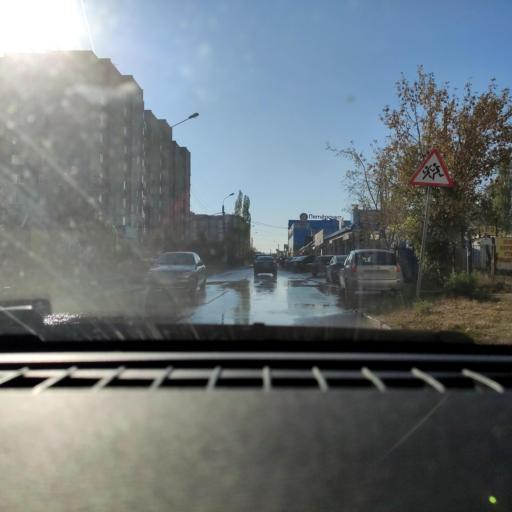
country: RU
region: Voronezj
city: Somovo
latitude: 51.7381
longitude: 39.2913
